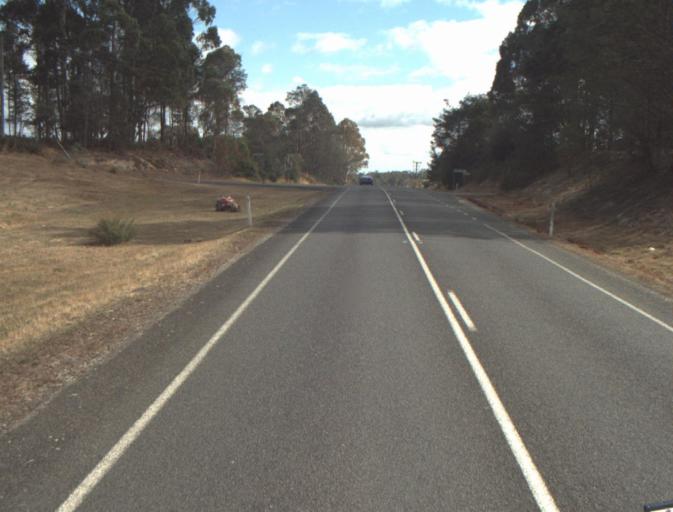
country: AU
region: Tasmania
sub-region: Launceston
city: Mayfield
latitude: -41.2872
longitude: 147.2178
